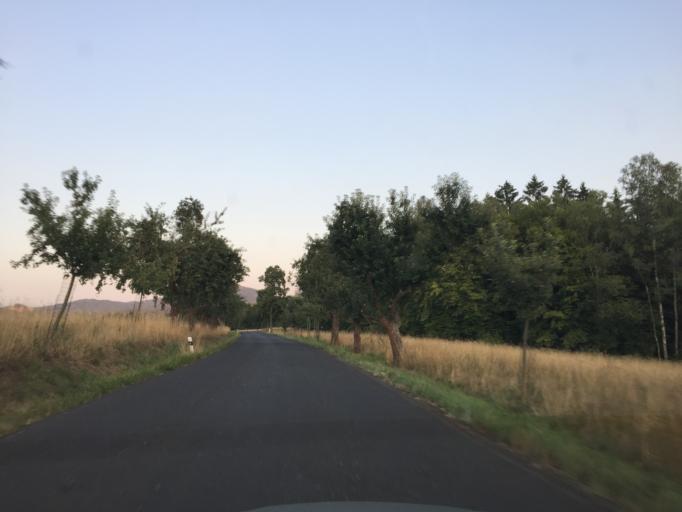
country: CZ
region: Ustecky
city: Ceska Kamenice
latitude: 50.8563
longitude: 14.3580
